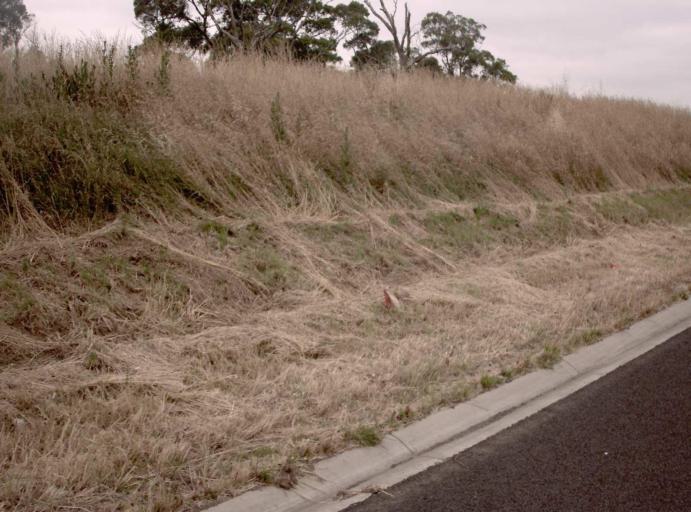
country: AU
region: Victoria
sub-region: Latrobe
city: Morwell
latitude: -38.2720
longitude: 146.3266
